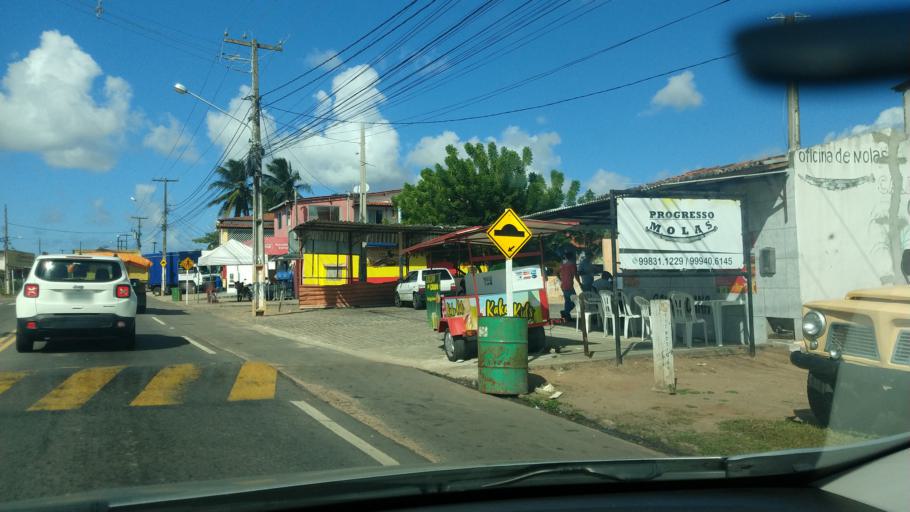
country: BR
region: Rio Grande do Norte
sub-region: Sao Goncalo Do Amarante
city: Sao Goncalo do Amarante
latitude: -5.7887
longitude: -35.2998
